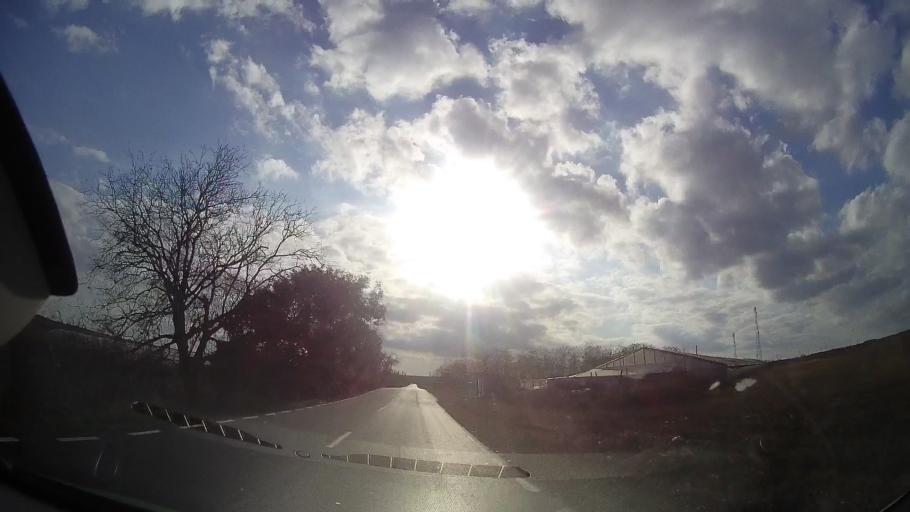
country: RO
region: Constanta
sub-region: Comuna Albesti
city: Albesti
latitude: 43.8109
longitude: 28.4370
